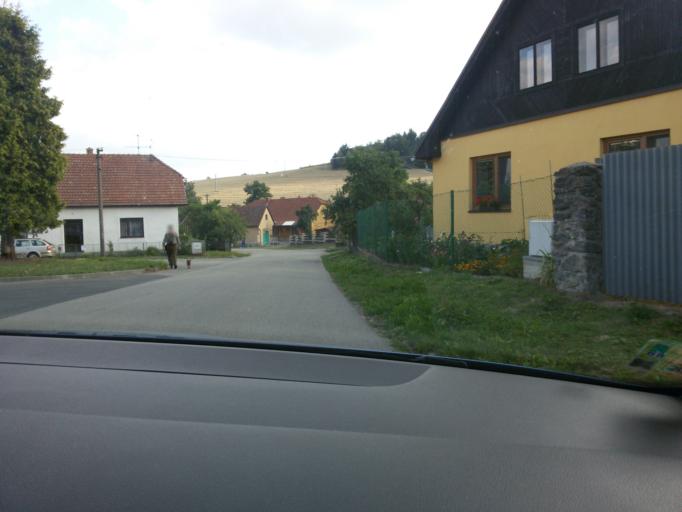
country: CZ
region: South Moravian
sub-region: Okres Brno-Venkov
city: Lomnice
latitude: 49.4617
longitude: 16.4267
